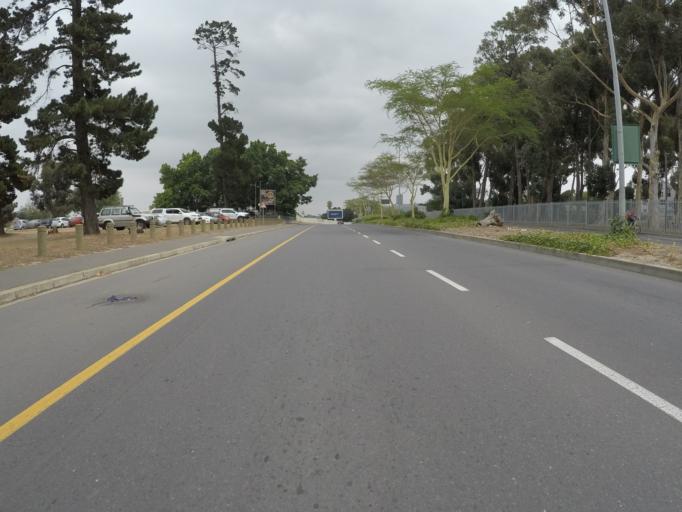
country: ZA
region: Western Cape
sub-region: City of Cape Town
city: Kraaifontein
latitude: -33.8724
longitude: 18.6444
